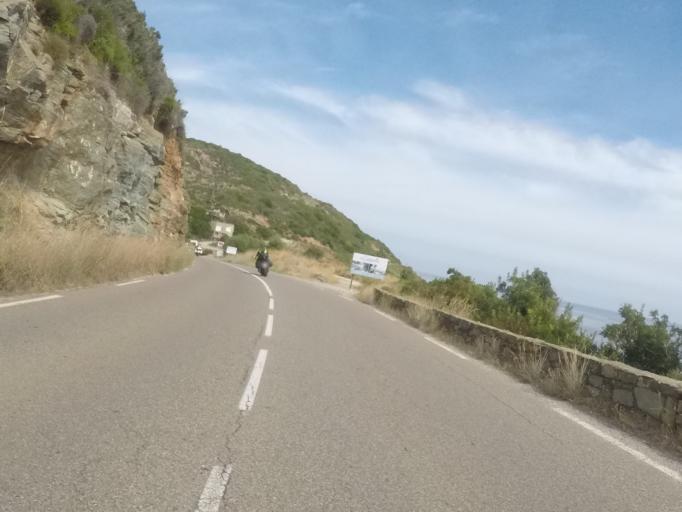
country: FR
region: Corsica
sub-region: Departement de la Haute-Corse
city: Brando
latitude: 42.8032
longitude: 9.4915
